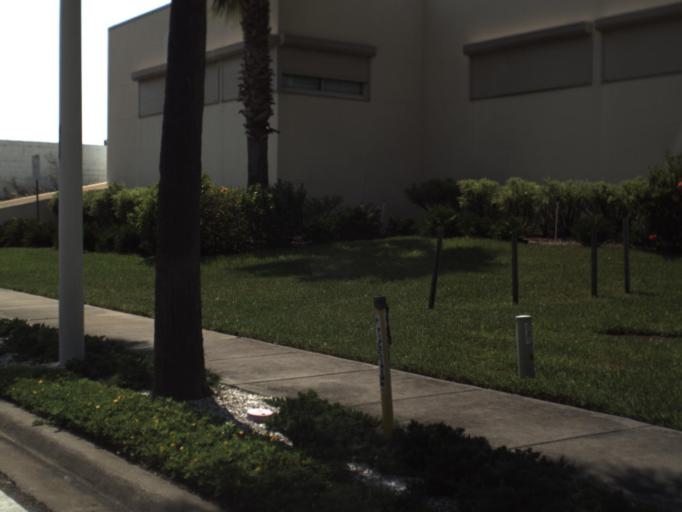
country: US
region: Florida
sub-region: Pinellas County
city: South Pasadena
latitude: 27.7442
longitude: -82.7481
